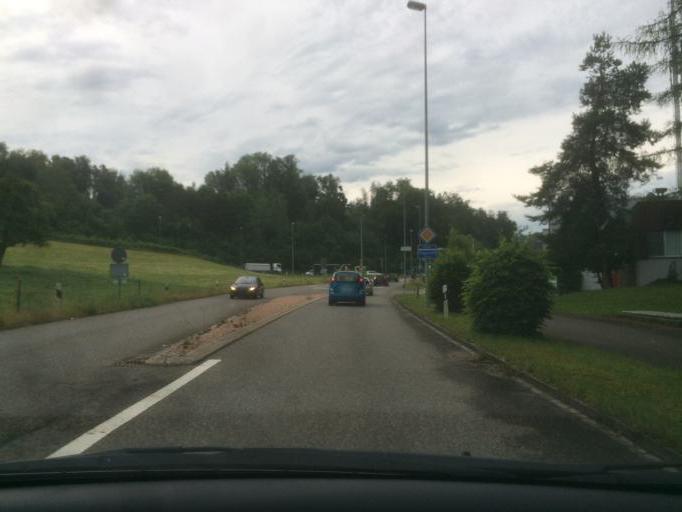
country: CH
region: Zurich
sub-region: Bezirk Uster
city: Uster / Ober-Uster
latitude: 47.3458
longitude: 8.7415
